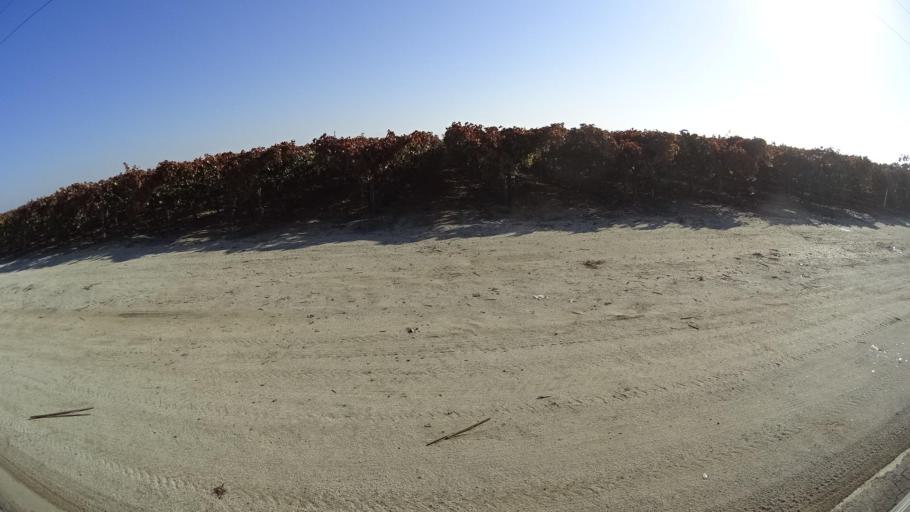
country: US
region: California
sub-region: Kern County
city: McFarland
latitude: 35.7208
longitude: -119.1694
